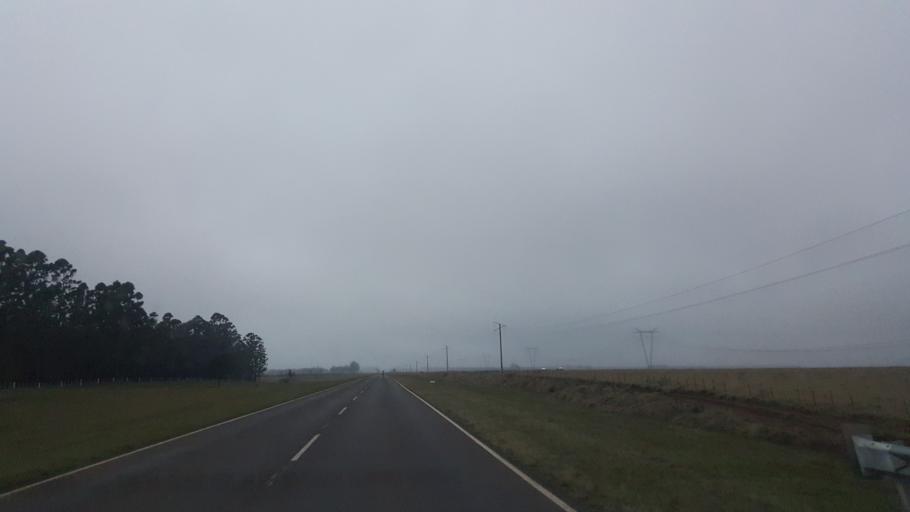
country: AR
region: Corrientes
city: Ituzaingo
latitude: -27.5897
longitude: -56.4810
